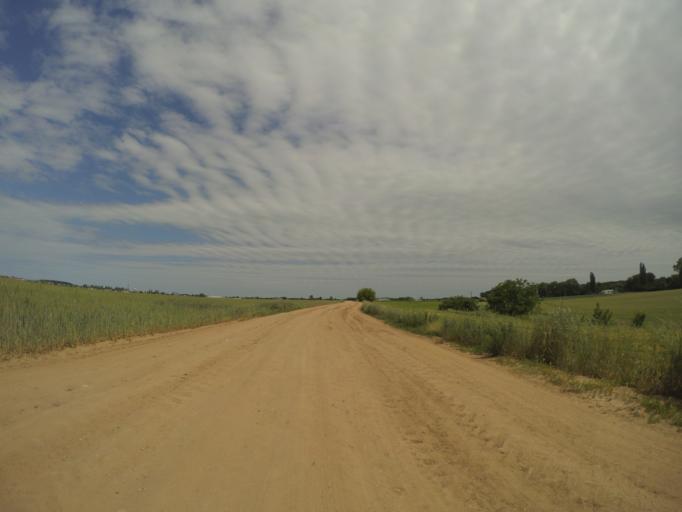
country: CZ
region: Central Bohemia
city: Lysa nad Labem
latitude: 50.1837
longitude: 14.8336
